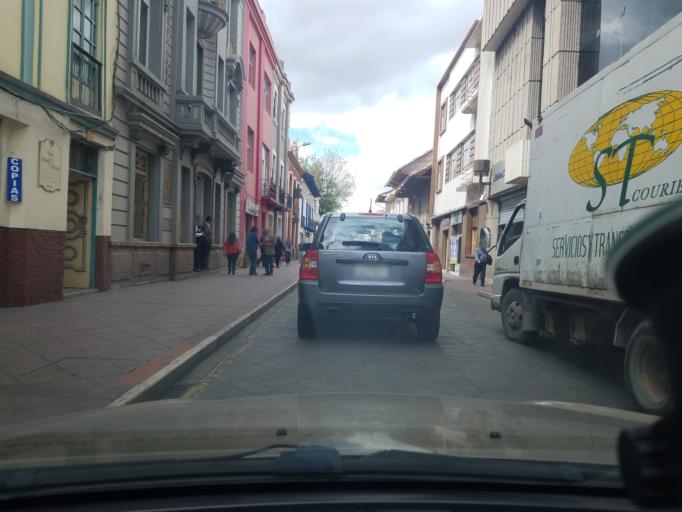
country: EC
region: Azuay
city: Cuenca
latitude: -2.8984
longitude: -79.0032
